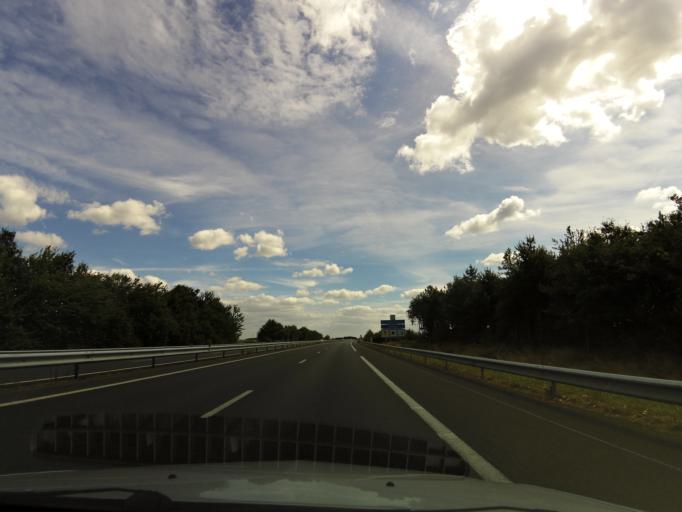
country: FR
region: Pays de la Loire
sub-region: Departement de la Vendee
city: Les Brouzils
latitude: 46.8935
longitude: -1.2984
